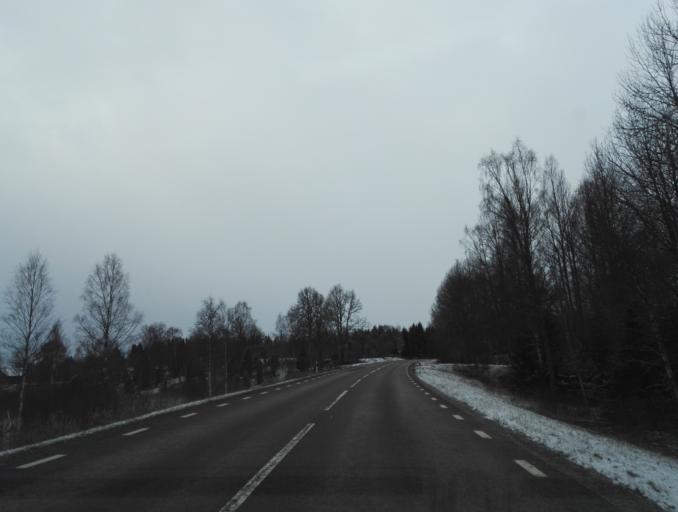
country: SE
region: Kalmar
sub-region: Hultsfreds Kommun
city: Virserum
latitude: 57.1973
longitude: 15.5119
